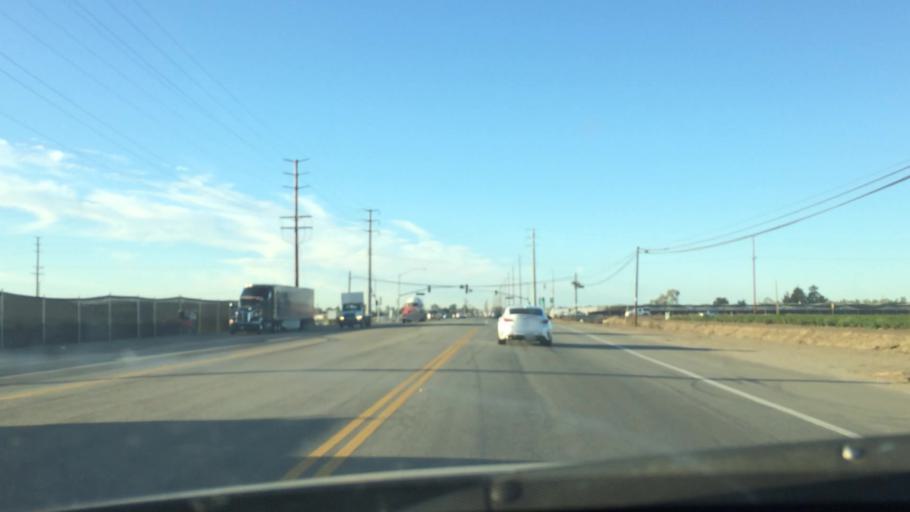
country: US
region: California
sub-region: Ventura County
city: El Rio
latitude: 34.2405
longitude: -119.1244
